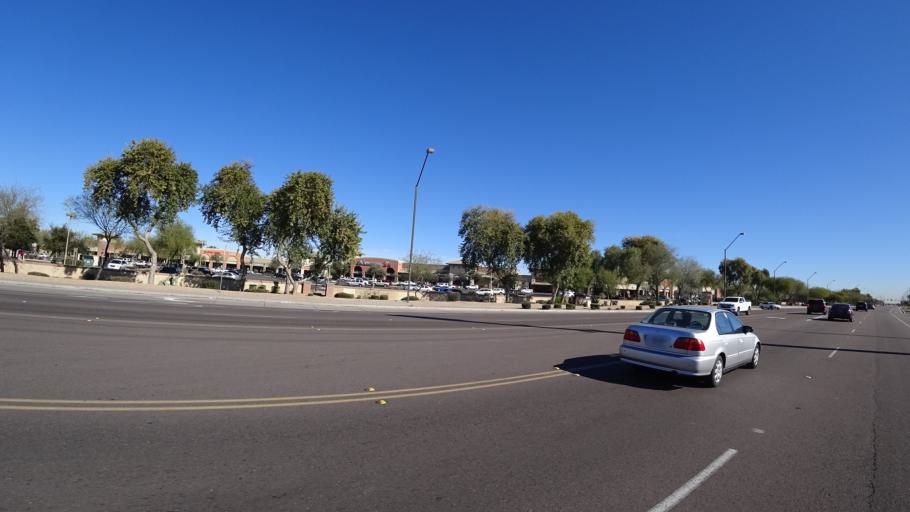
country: US
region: Arizona
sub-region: Maricopa County
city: Litchfield Park
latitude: 33.4932
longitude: -112.3393
